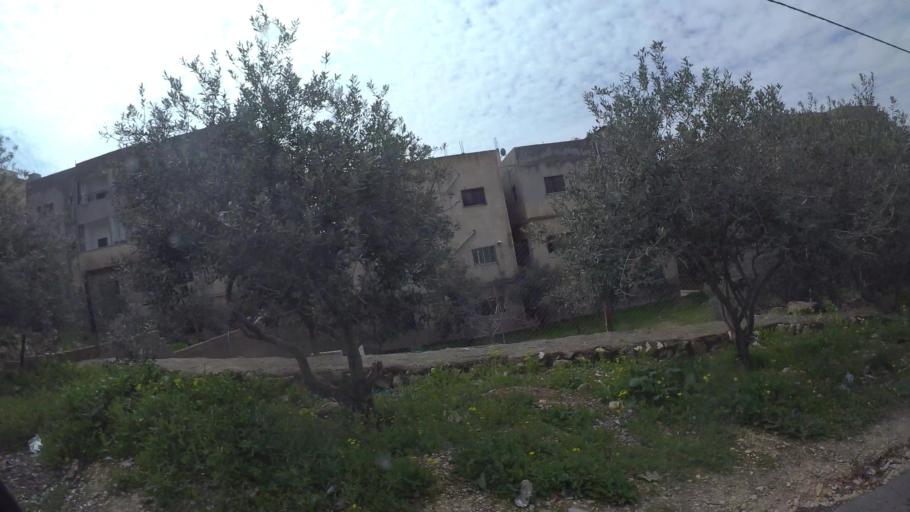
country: JO
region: Amman
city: Al Jubayhah
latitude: 32.0647
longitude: 35.8312
